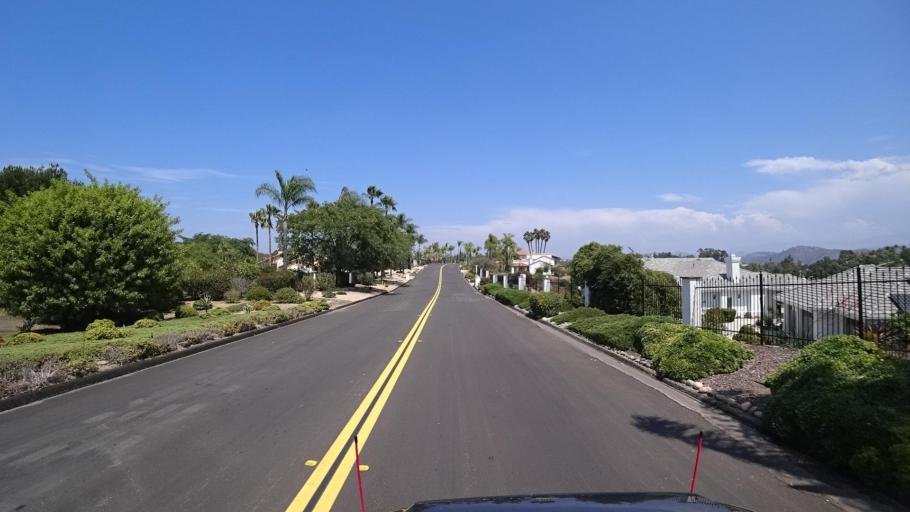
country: US
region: California
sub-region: San Diego County
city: Bonsall
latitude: 33.3108
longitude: -117.2170
